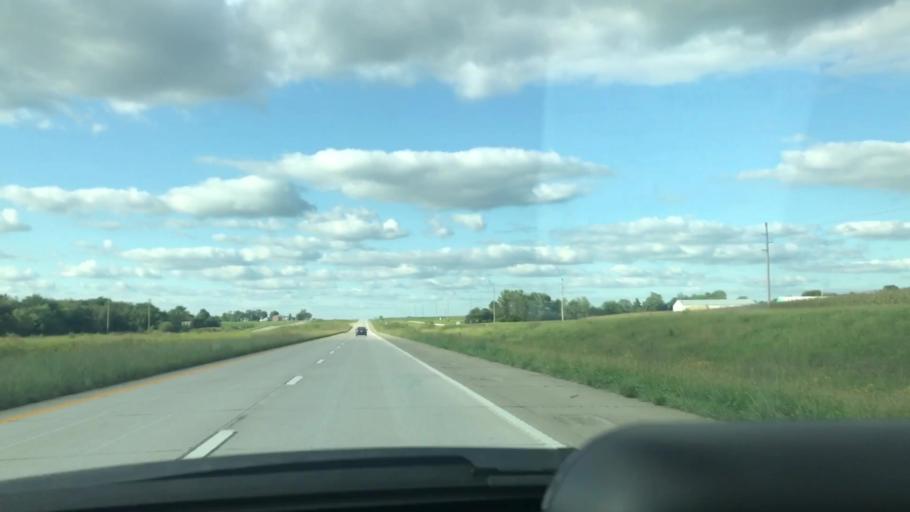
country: US
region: Missouri
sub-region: Benton County
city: Cole Camp
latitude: 38.4929
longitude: -93.2735
